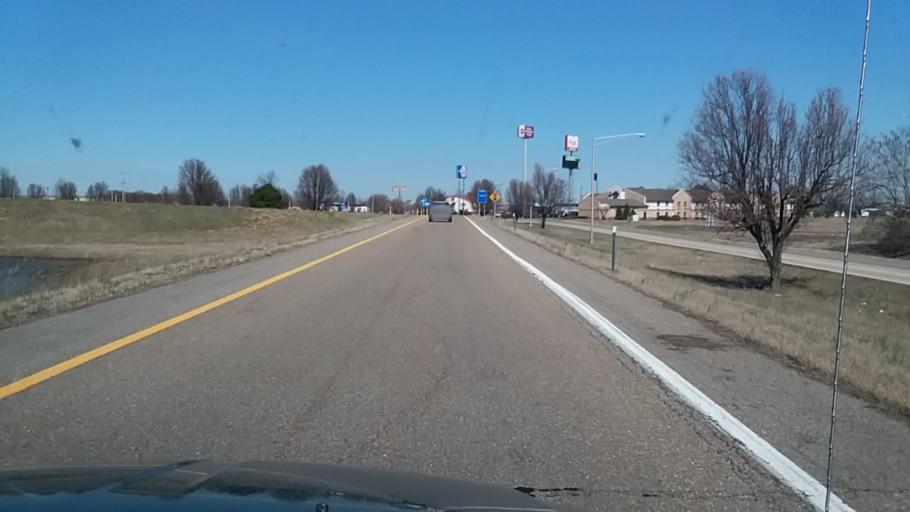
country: US
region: Missouri
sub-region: Scott County
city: Sikeston
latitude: 36.8902
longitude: -89.5326
